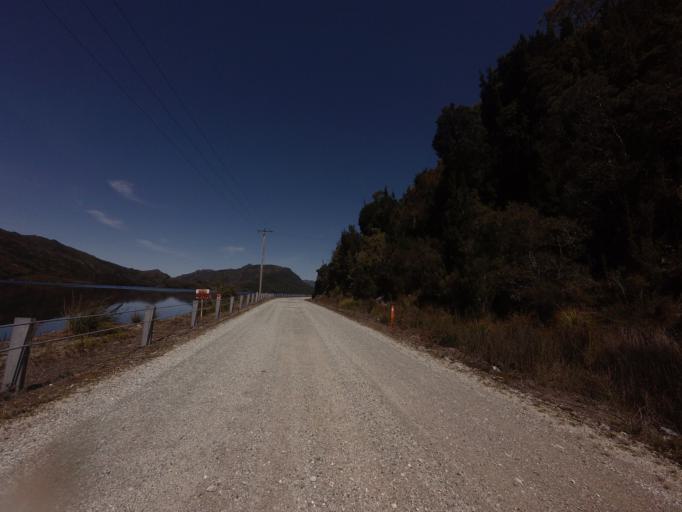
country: AU
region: Tasmania
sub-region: West Coast
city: Queenstown
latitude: -42.7736
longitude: 145.9850
